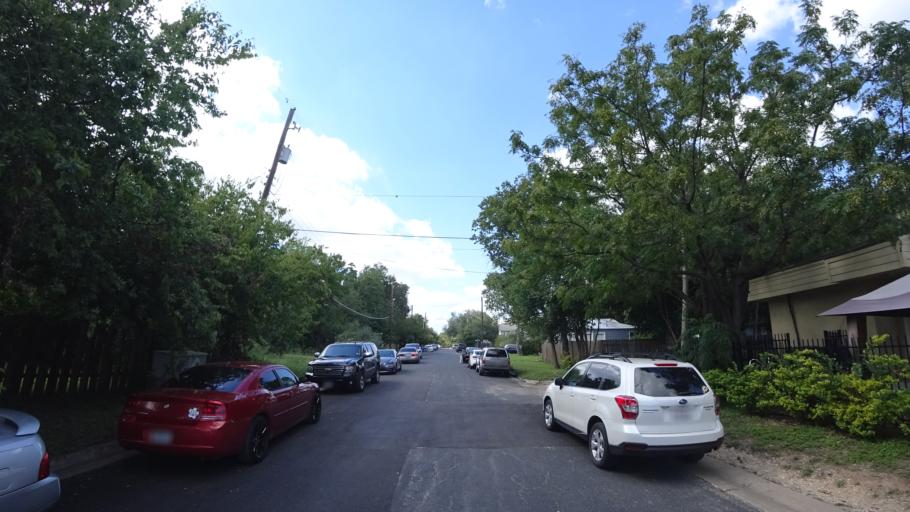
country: US
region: Texas
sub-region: Travis County
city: Austin
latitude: 30.3116
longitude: -97.7174
